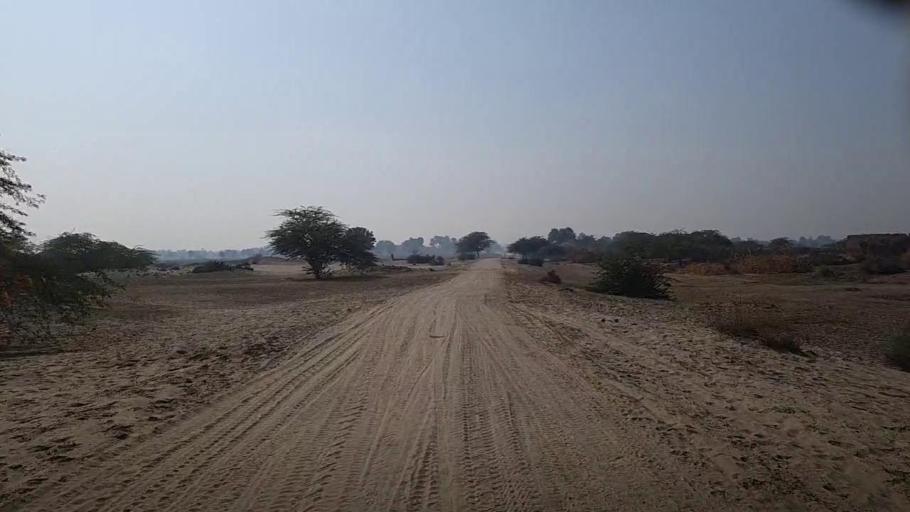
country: PK
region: Sindh
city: Bozdar
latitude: 27.2175
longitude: 68.5809
